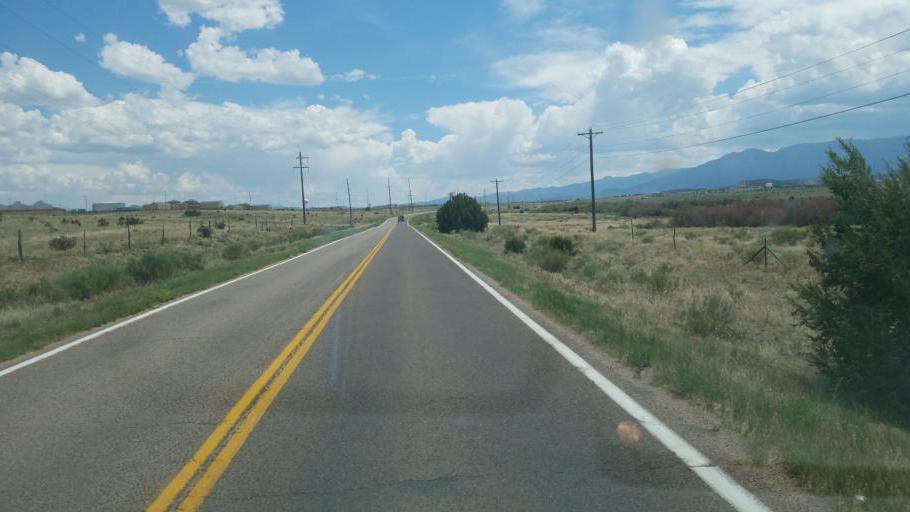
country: US
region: Colorado
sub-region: Fremont County
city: Florence
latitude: 38.3708
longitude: -105.1084
